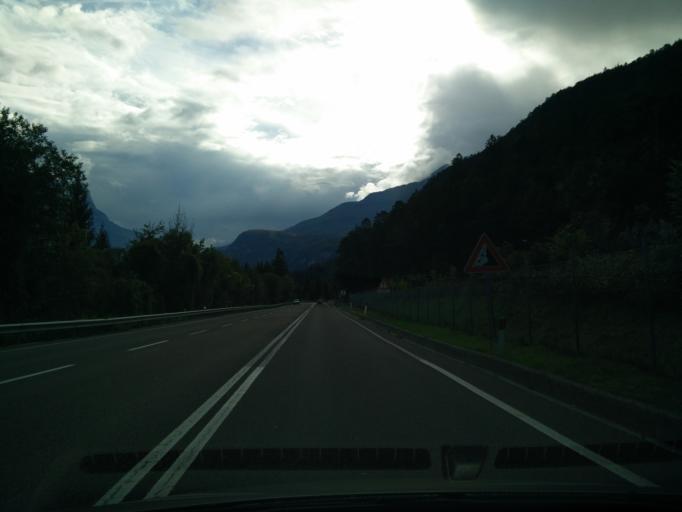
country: IT
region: Veneto
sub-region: Provincia di Belluno
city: Pieve di Cadore
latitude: 46.4173
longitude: 12.3742
